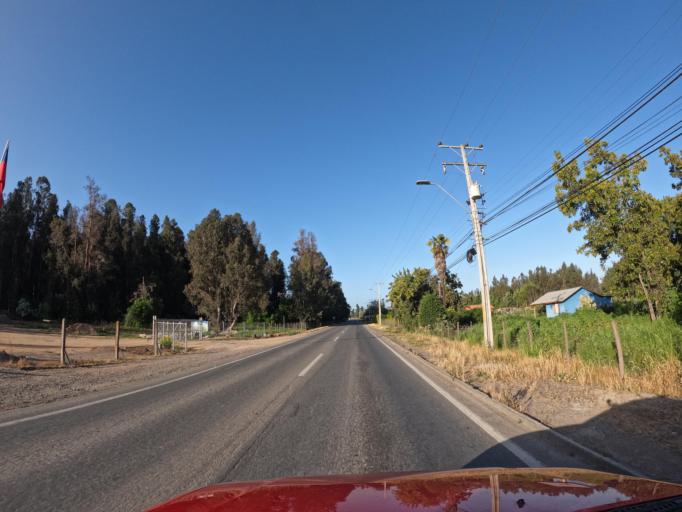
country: CL
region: O'Higgins
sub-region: Provincia de Colchagua
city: Santa Cruz
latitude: -34.5241
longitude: -71.3829
